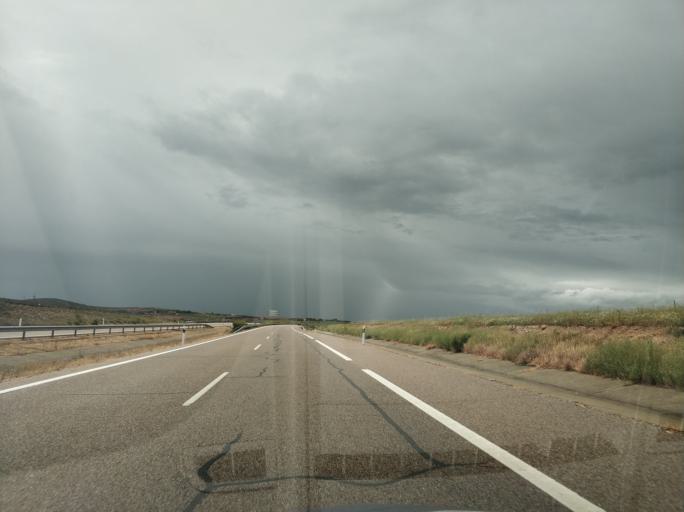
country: ES
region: Castille and Leon
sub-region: Provincia de Salamanca
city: Aldeatejada
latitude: 40.9248
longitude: -5.6715
